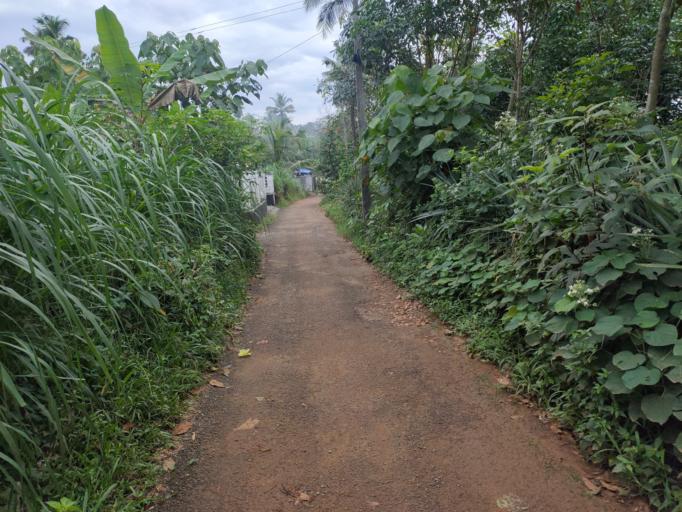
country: IN
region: Kerala
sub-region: Ernakulam
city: Kotamangalam
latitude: 9.9987
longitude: 76.6404
